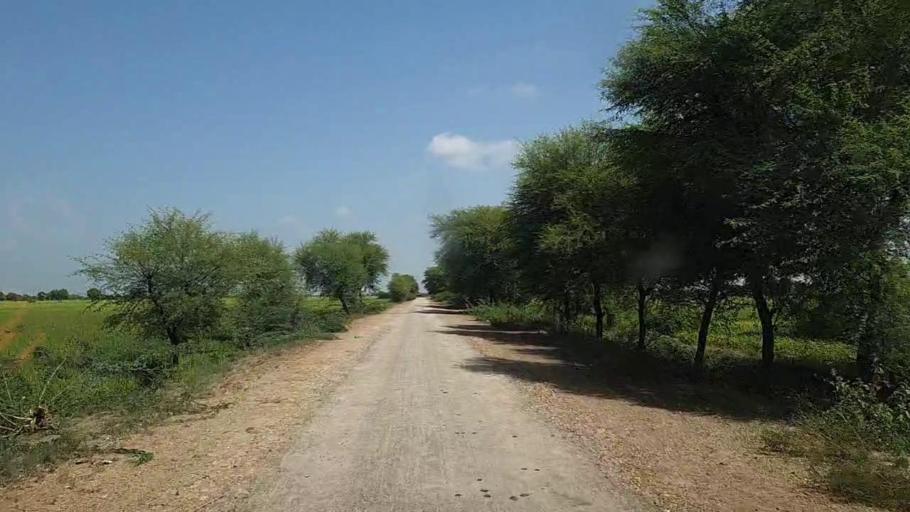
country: PK
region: Sindh
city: Kario
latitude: 24.6433
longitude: 68.5650
